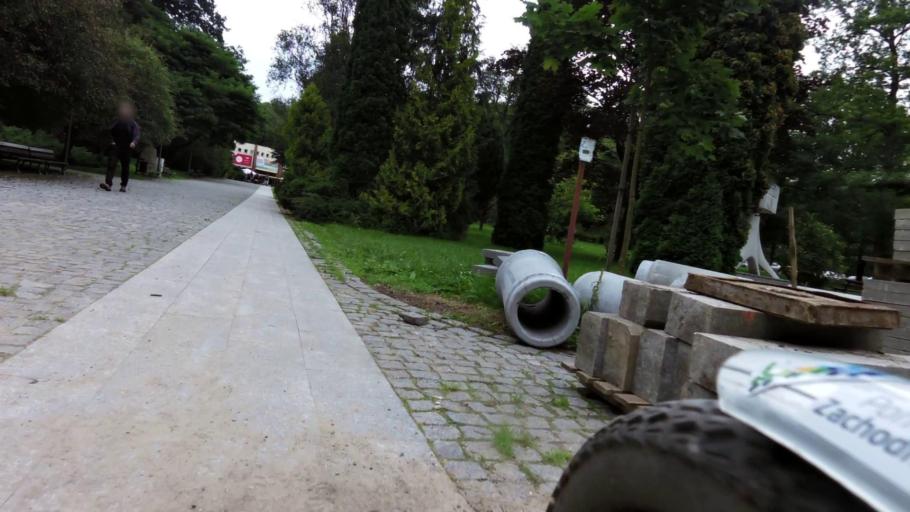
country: PL
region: West Pomeranian Voivodeship
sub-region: Koszalin
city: Koszalin
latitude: 54.1920
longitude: 16.1871
